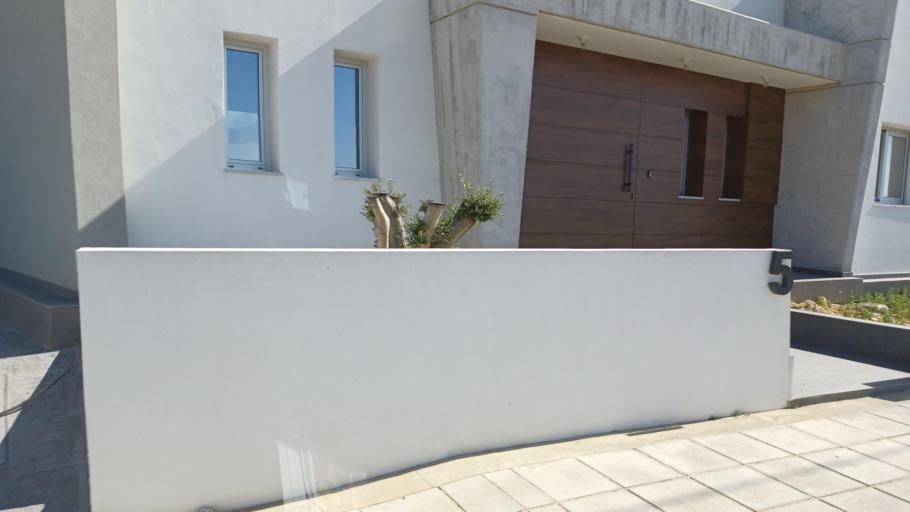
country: CY
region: Lefkosia
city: Kokkinotrimithia
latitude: 35.1484
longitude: 33.2141
